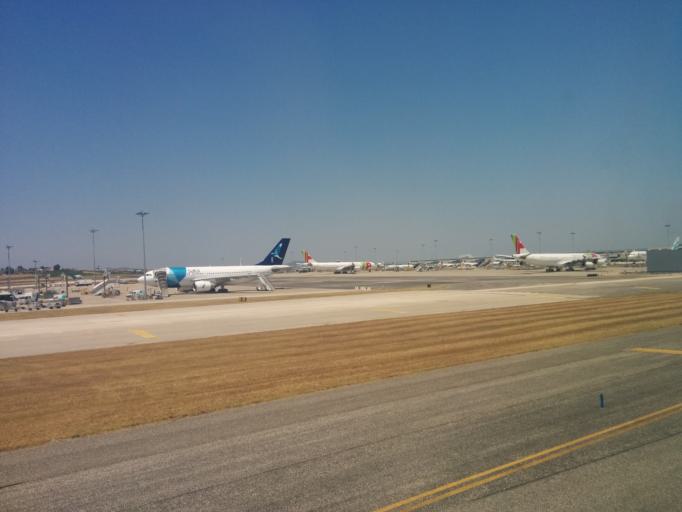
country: PT
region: Lisbon
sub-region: Odivelas
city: Olival do Basto
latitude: 38.7658
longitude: -9.1392
